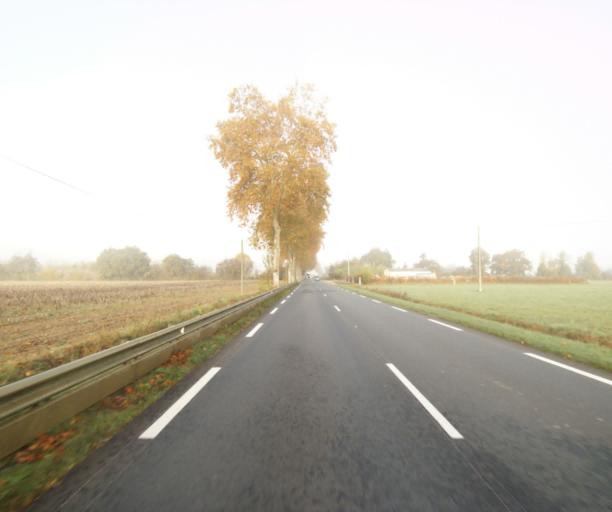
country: FR
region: Midi-Pyrenees
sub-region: Departement de la Haute-Garonne
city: Villemur-sur-Tarn
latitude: 43.9333
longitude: 1.4898
